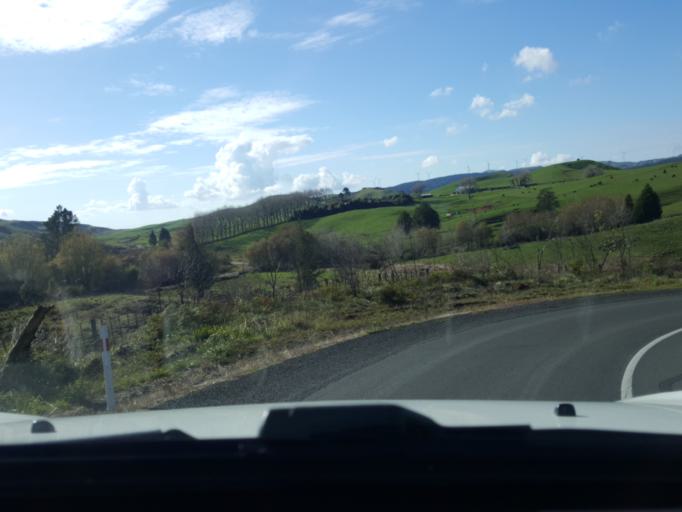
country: NZ
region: Waikato
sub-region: Waikato District
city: Raglan
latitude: -37.9050
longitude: 174.9009
